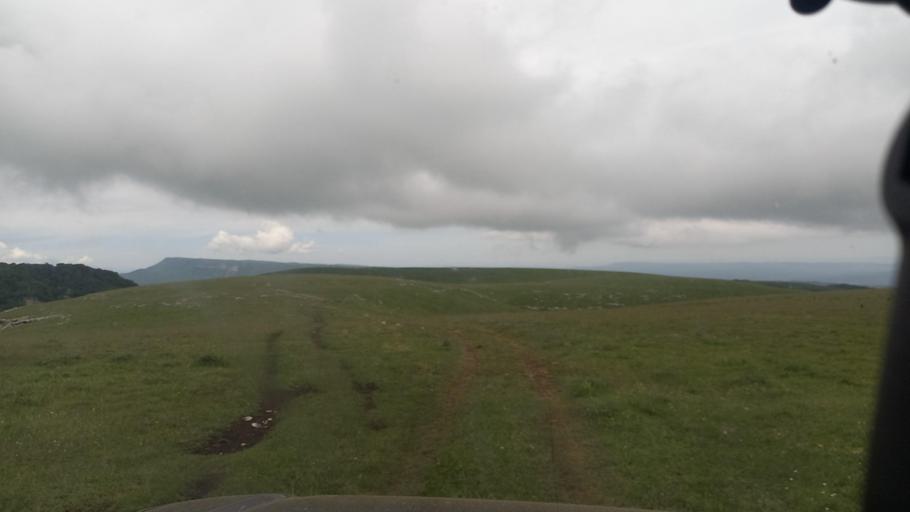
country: RU
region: Karachayevo-Cherkesiya
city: Pregradnaya
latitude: 43.9837
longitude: 41.2915
